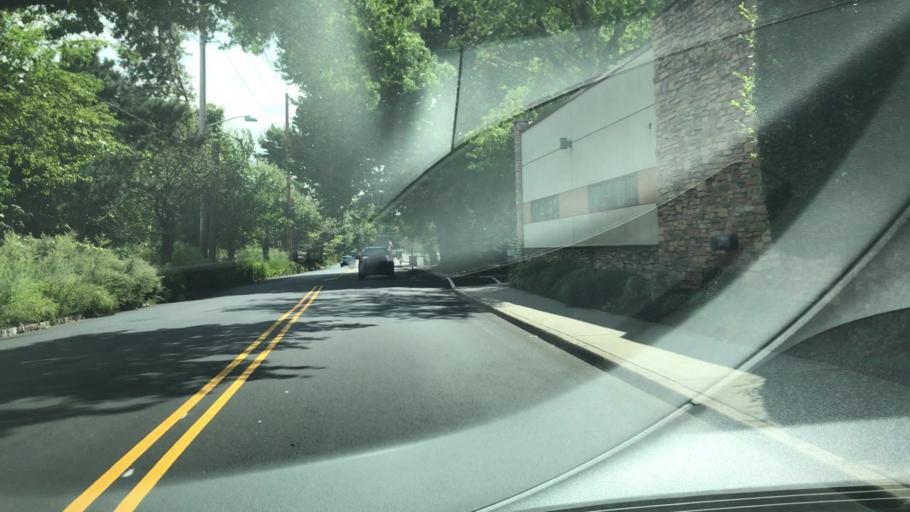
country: US
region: New Jersey
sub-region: Bergen County
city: Bergenfield
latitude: 40.9234
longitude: -73.9993
